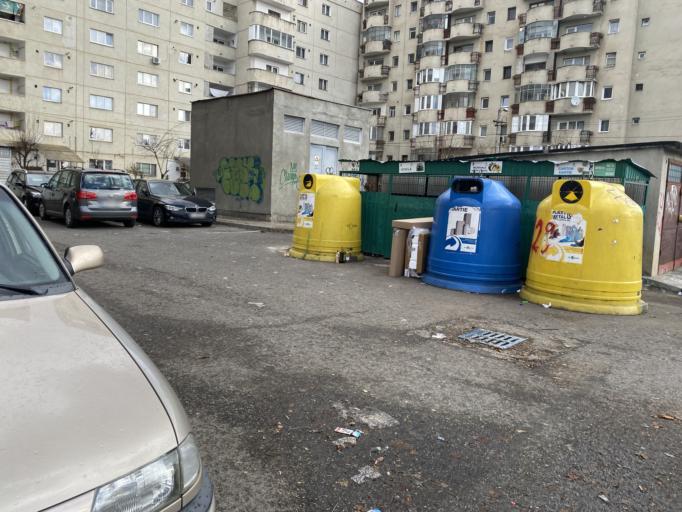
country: RO
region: Cluj
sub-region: Municipiul Cluj-Napoca
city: Cluj-Napoca
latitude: 46.7598
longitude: 23.5636
